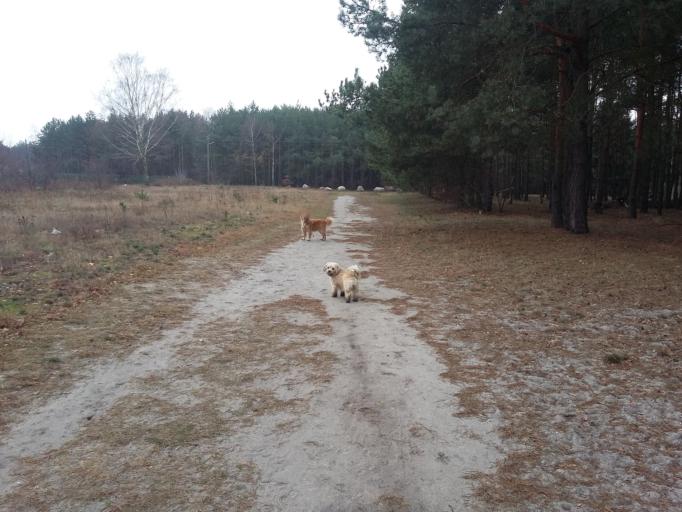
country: PL
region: Lodz Voivodeship
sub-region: Powiat pabianicki
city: Ksawerow
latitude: 51.7280
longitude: 19.3829
